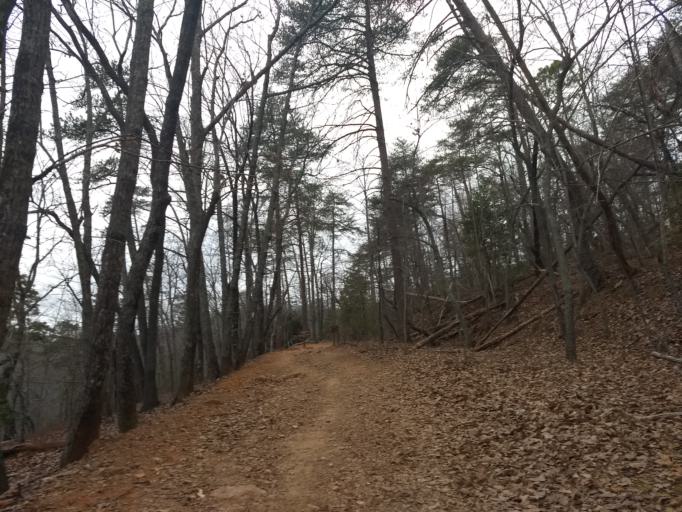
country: US
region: South Carolina
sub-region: Greenville County
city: Travelers Rest
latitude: 34.9424
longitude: -82.3989
